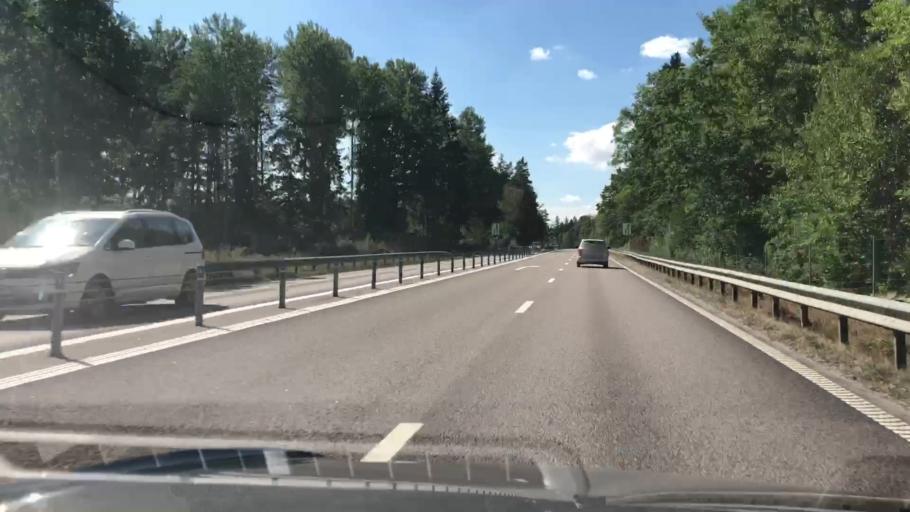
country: SE
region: Kalmar
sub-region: Monsteras Kommun
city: Timmernabben
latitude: 56.9079
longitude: 16.3809
